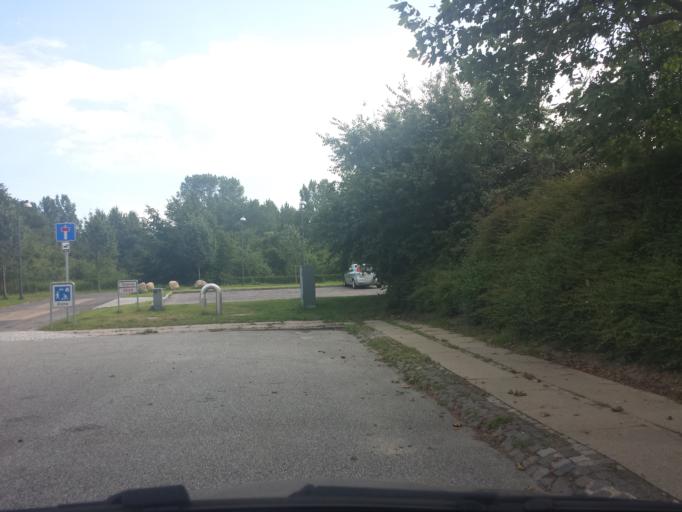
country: DK
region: Capital Region
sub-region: Ballerup Kommune
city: Ballerup
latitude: 55.7093
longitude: 12.3945
